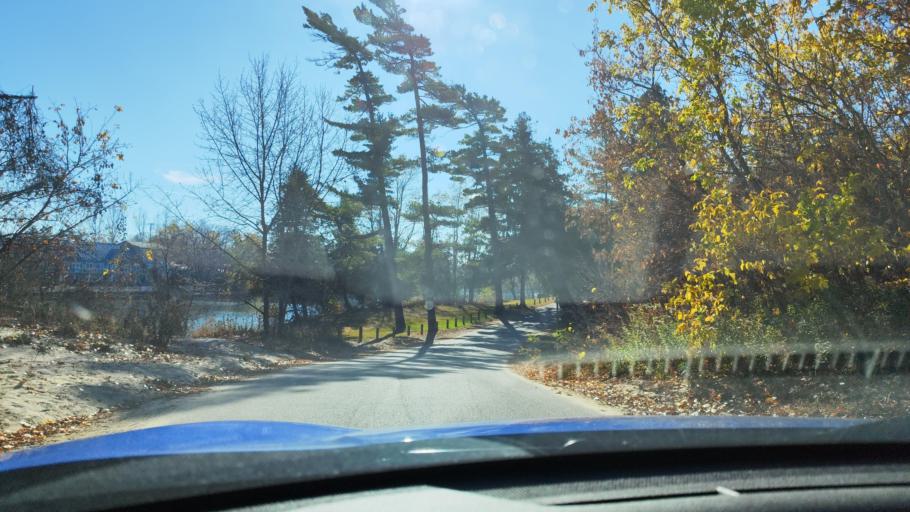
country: CA
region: Ontario
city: Wasaga Beach
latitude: 44.5265
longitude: -80.0161
